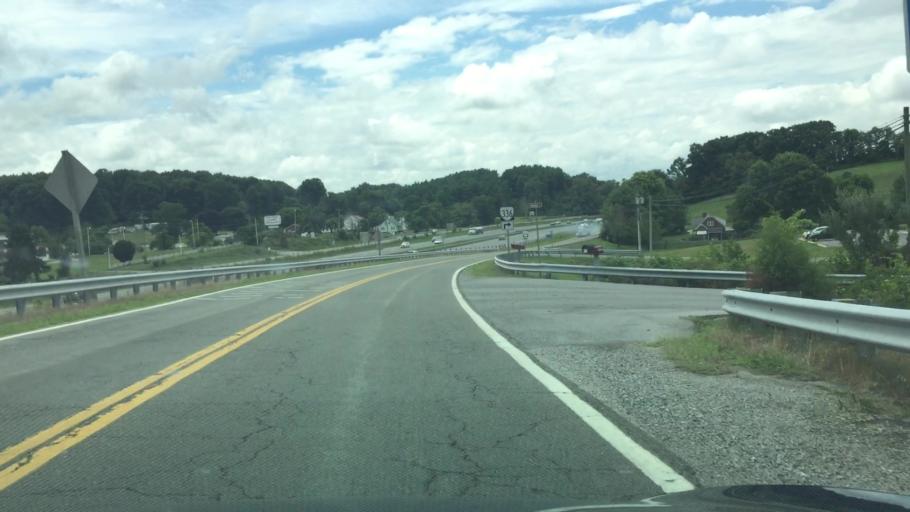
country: US
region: Virginia
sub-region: Wythe County
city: Wytheville
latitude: 36.9380
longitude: -80.9961
